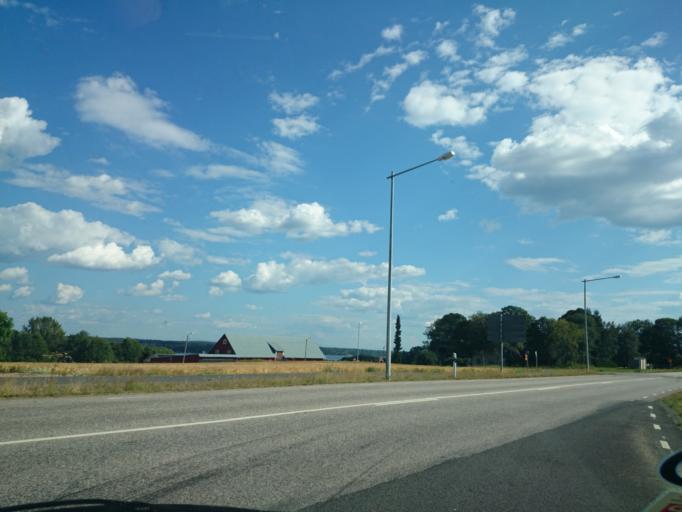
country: SE
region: Joenkoeping
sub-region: Varnamo Kommun
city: Varnamo
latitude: 57.1668
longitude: 14.0333
